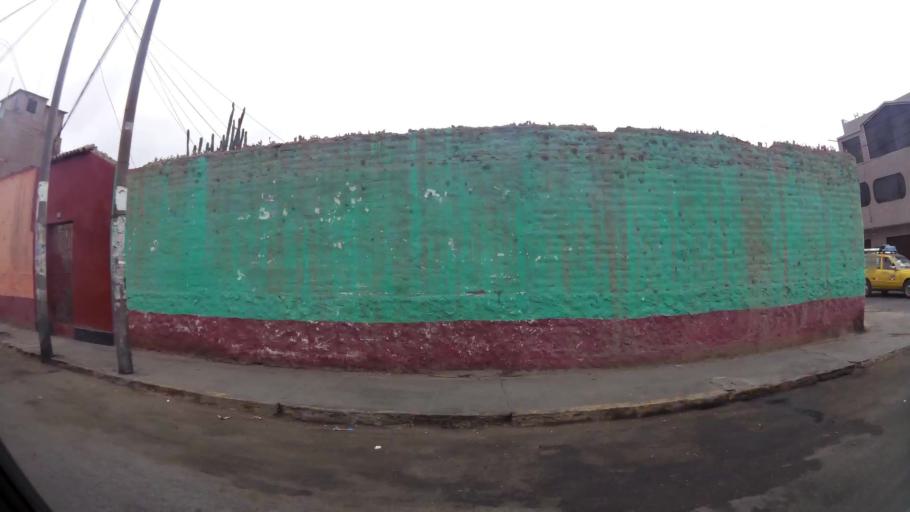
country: PE
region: La Libertad
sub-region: Provincia de Trujillo
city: Trujillo
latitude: -8.1158
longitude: -79.0172
